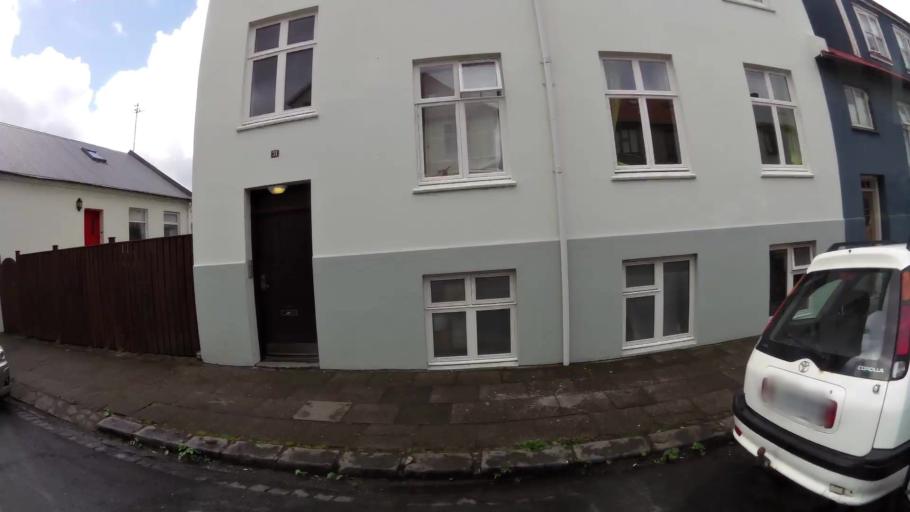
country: IS
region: Capital Region
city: Seltjarnarnes
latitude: 64.1505
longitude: -21.9565
